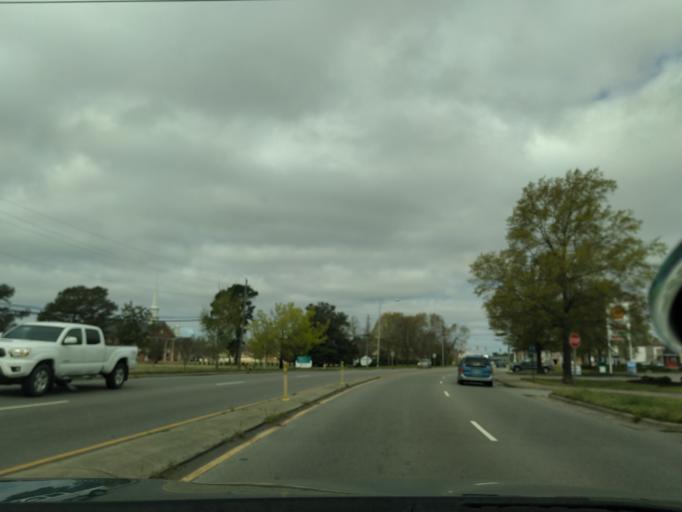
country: US
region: North Carolina
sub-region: Chowan County
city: Edenton
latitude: 36.0711
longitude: -76.6095
